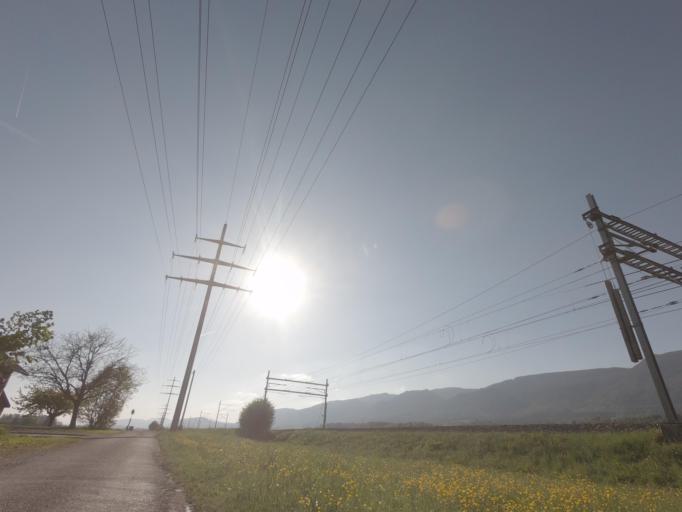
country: CH
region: Solothurn
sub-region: Bezirk Lebern
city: Langendorf
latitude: 47.2071
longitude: 7.4897
